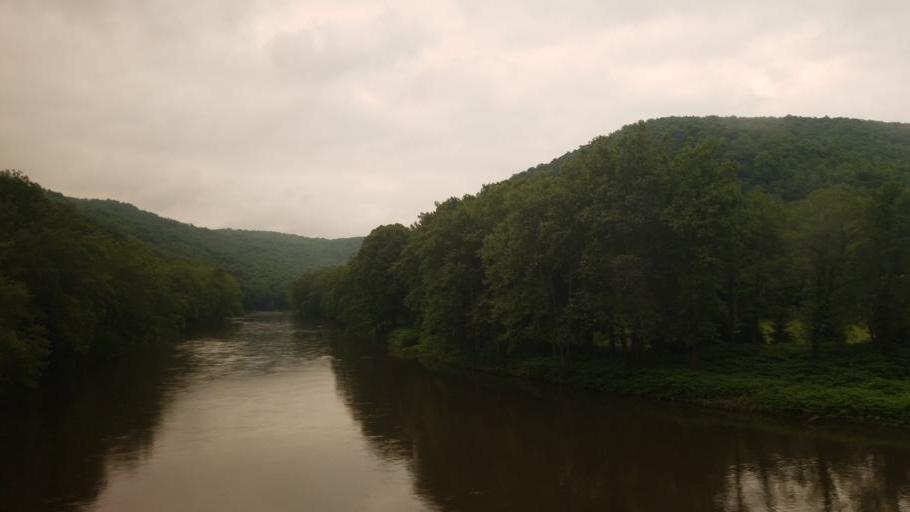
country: US
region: Pennsylvania
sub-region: Fayette County
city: South Connellsville
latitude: 39.9683
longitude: -79.5129
